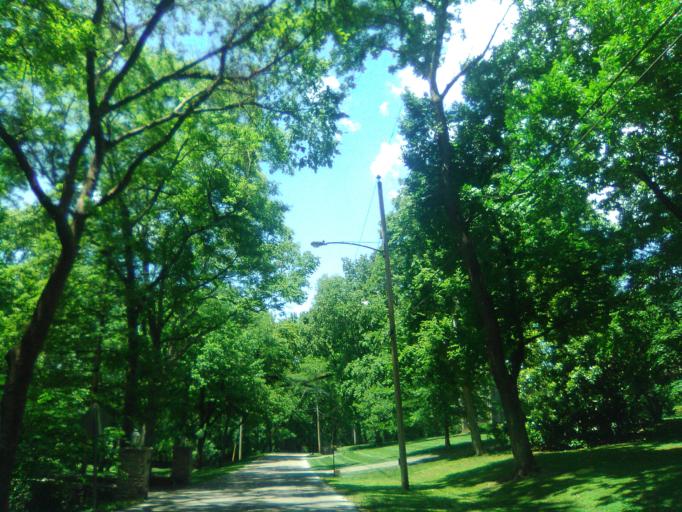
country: US
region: Tennessee
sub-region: Davidson County
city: Belle Meade
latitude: 36.1127
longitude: -86.8593
